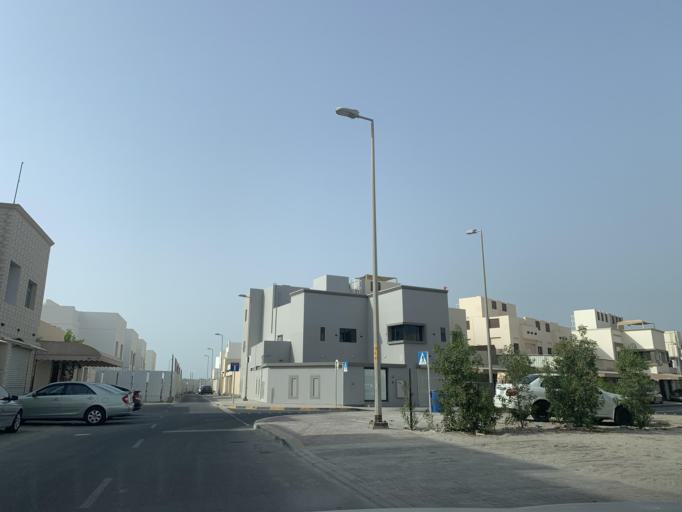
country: BH
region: Manama
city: Jidd Hafs
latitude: 26.2263
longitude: 50.4425
